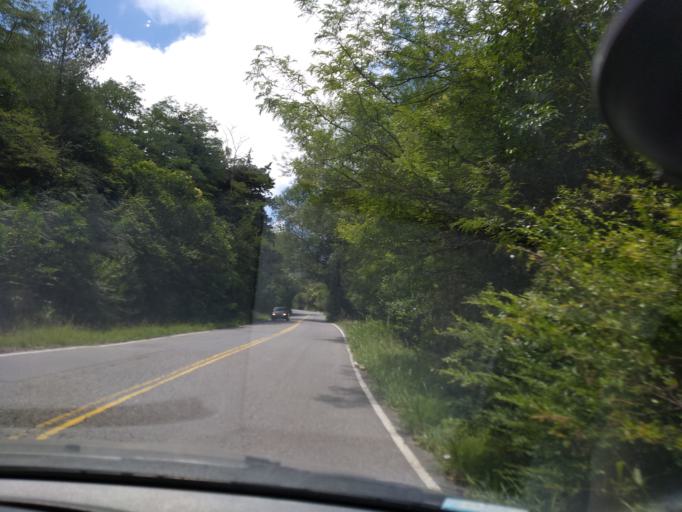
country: AR
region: Cordoba
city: Cuesta Blanca
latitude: -31.6016
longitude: -64.5469
